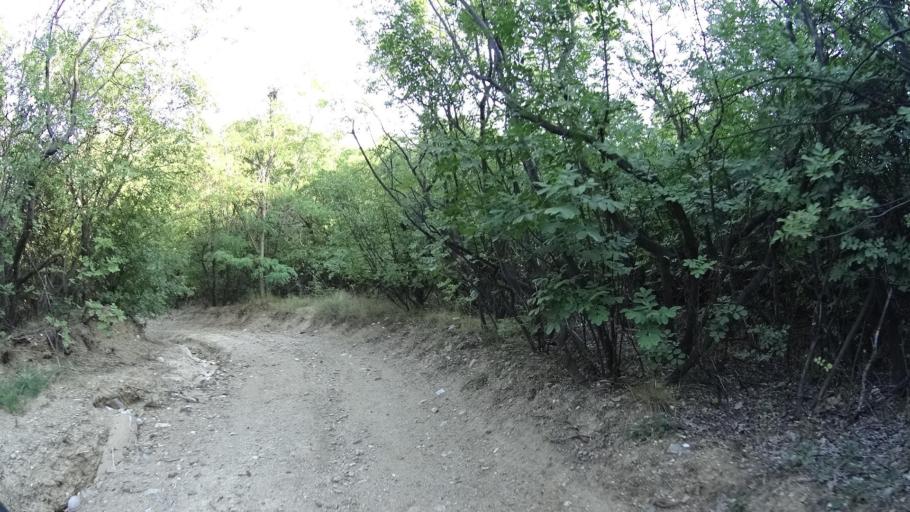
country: BG
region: Plovdiv
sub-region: Obshtina Plovdiv
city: Plovdiv
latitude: 42.0552
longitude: 24.6944
